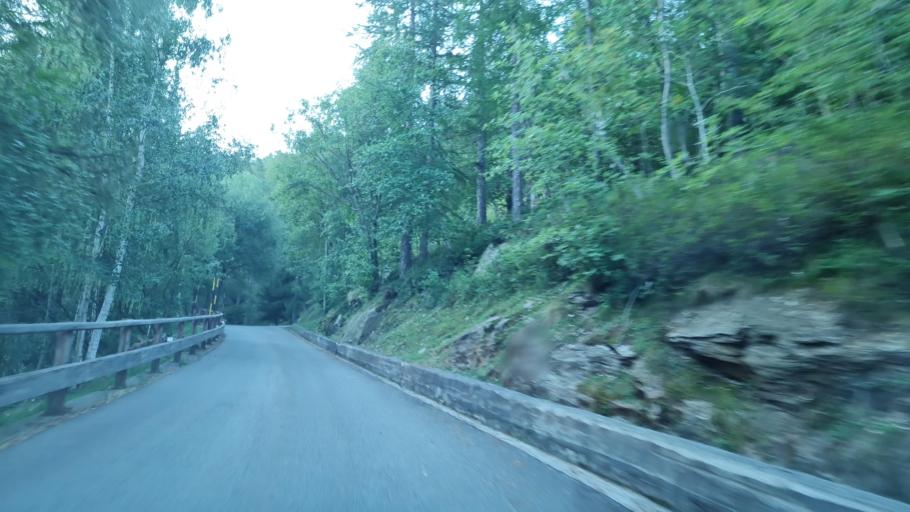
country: IT
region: Aosta Valley
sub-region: Valle d'Aosta
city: Fontainemore
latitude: 45.6335
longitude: 7.8600
